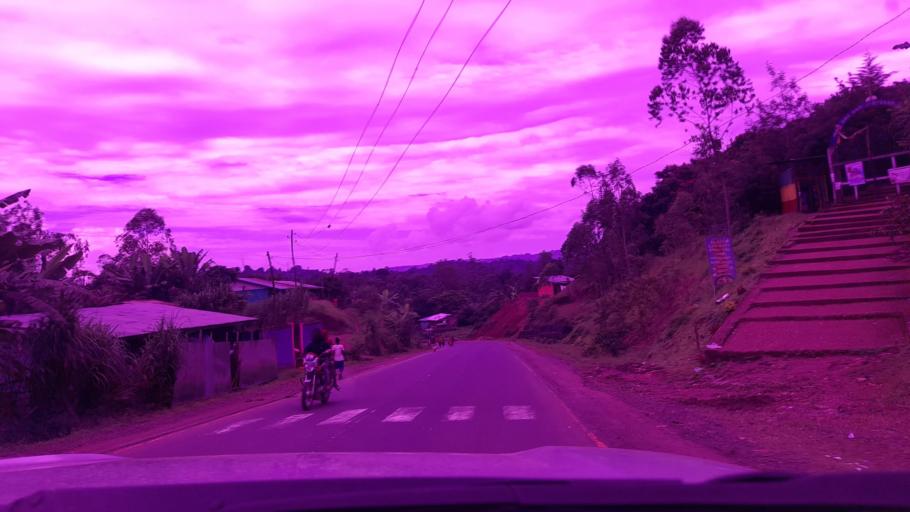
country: ET
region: Southern Nations, Nationalities, and People's Region
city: Mizan Teferi
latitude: 7.0029
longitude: 35.6018
